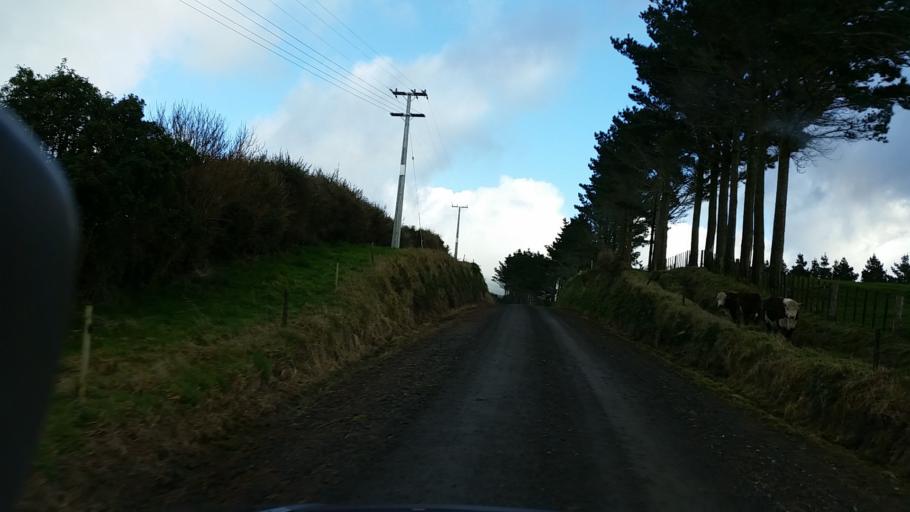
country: NZ
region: Taranaki
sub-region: South Taranaki District
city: Eltham
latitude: -39.3382
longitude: 174.1856
